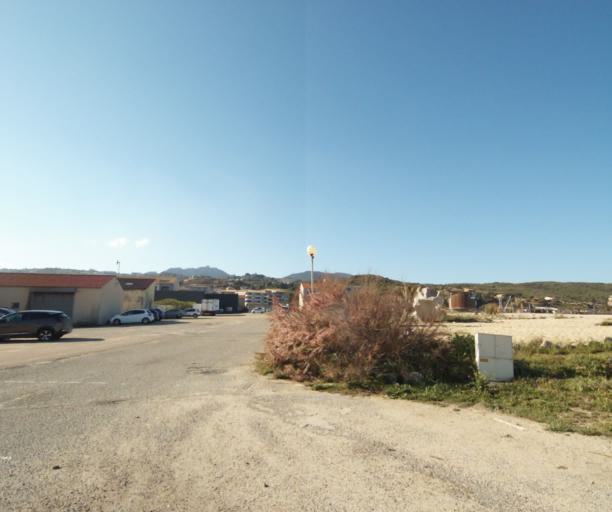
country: FR
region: Corsica
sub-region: Departement de la Corse-du-Sud
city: Propriano
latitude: 41.6769
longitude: 8.8973
